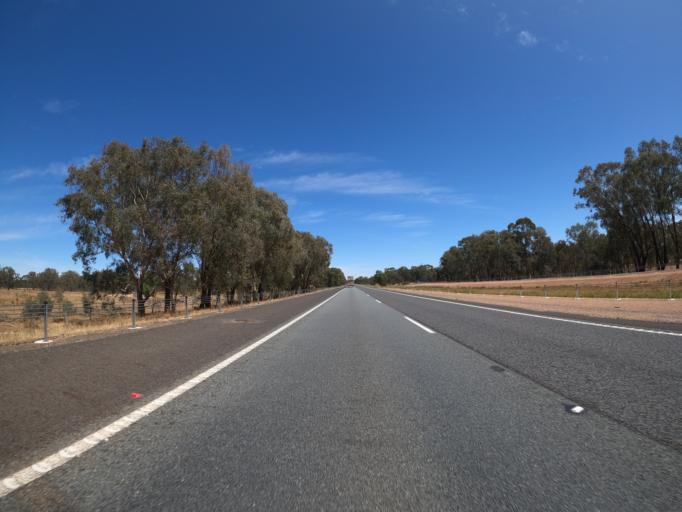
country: AU
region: Victoria
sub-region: Benalla
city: Benalla
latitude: -36.6000
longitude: 145.8577
